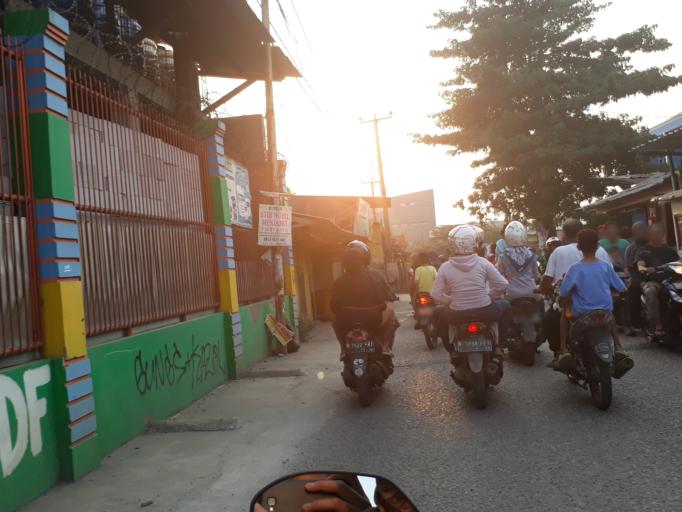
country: ID
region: West Java
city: Bekasi
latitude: -6.2436
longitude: 107.0449
